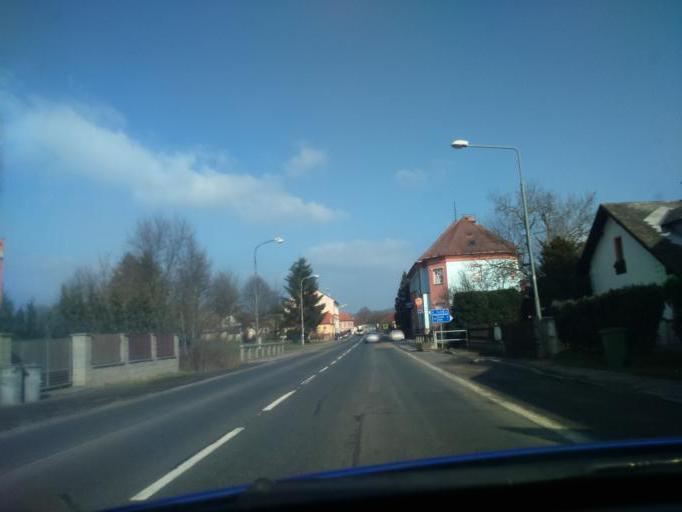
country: CZ
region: Plzensky
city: Stankov
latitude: 49.5510
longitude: 13.0661
